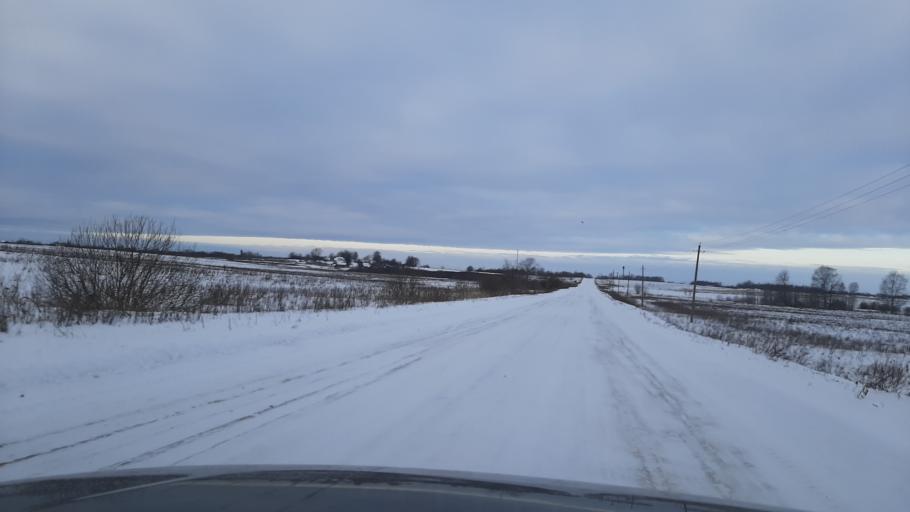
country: RU
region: Kostroma
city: Kosmynino
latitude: 57.4445
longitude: 40.9330
